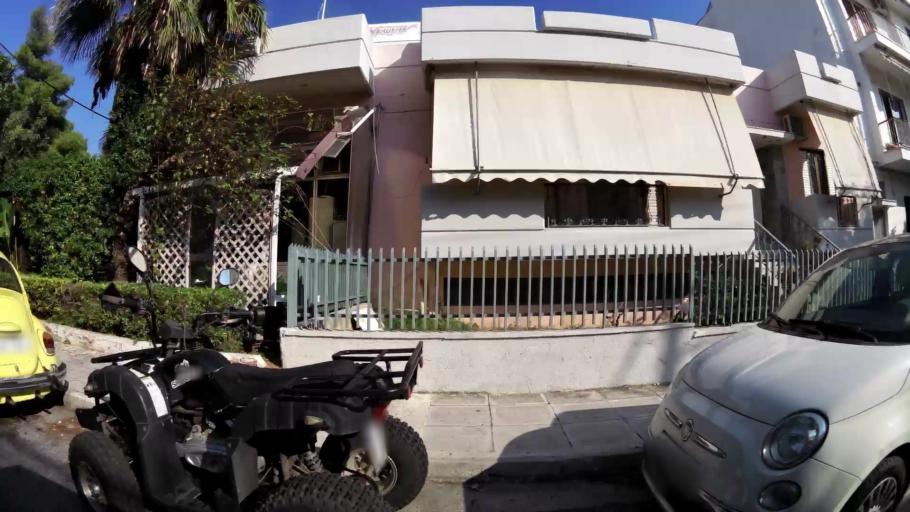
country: GR
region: Attica
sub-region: Nomarchia Athinas
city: Argyroupoli
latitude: 37.9143
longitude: 23.7506
